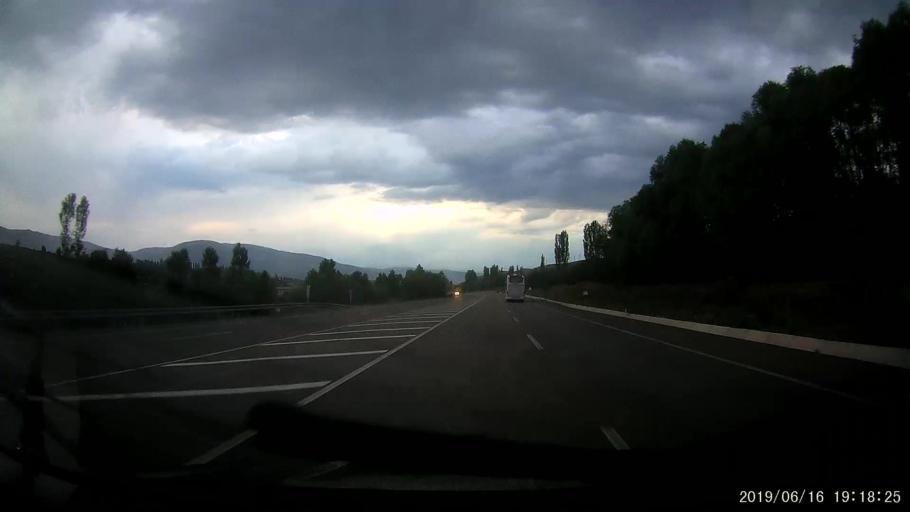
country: TR
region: Sivas
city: Akincilar
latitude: 40.0952
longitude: 38.4584
